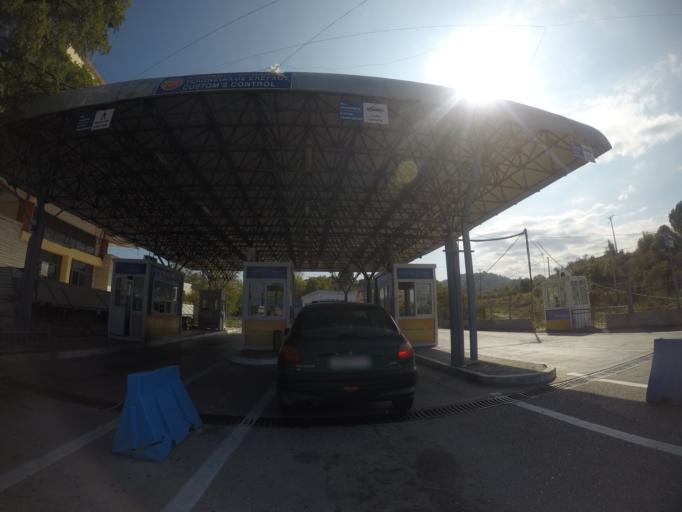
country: AL
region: Gjirokaster
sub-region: Rrethi i Gjirokastres
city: Kakavije
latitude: 39.9124
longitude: 20.3567
